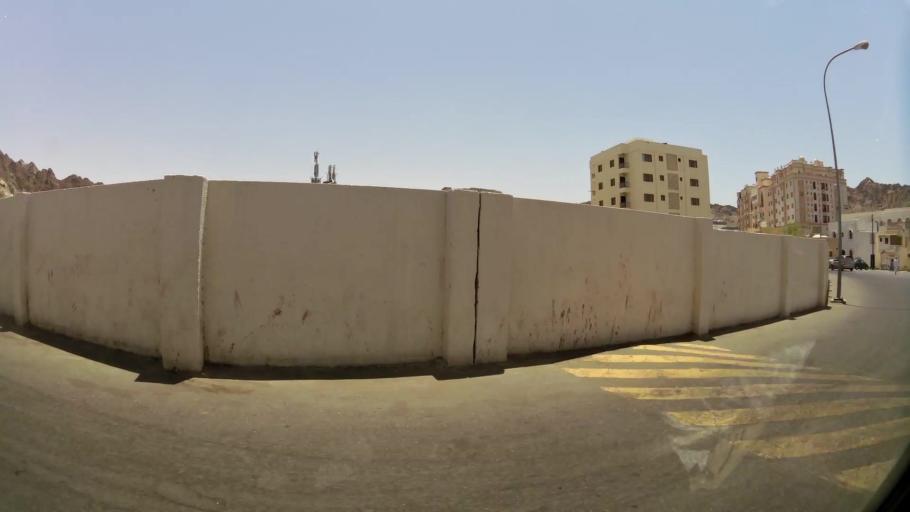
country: OM
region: Muhafazat Masqat
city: Muscat
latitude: 23.6214
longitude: 58.5559
